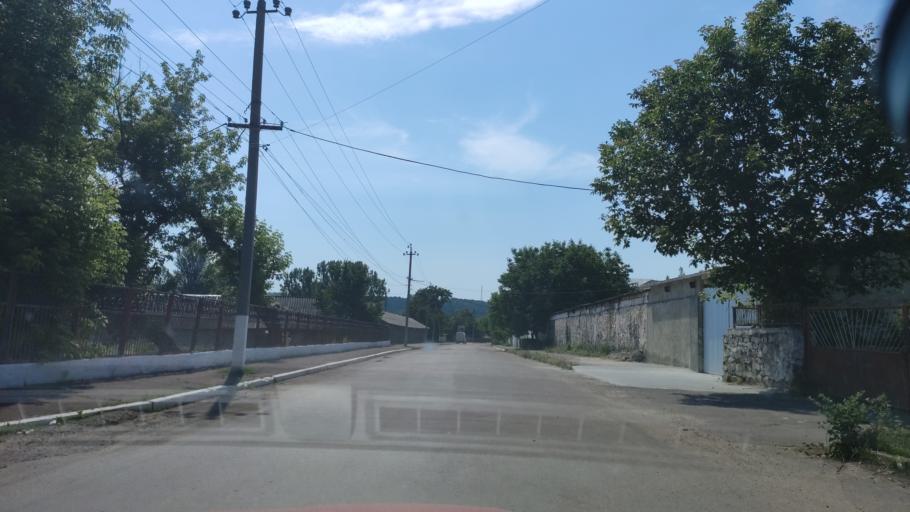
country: MD
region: Raionul Soroca
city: Soroca
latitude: 48.1726
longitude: 28.3147
